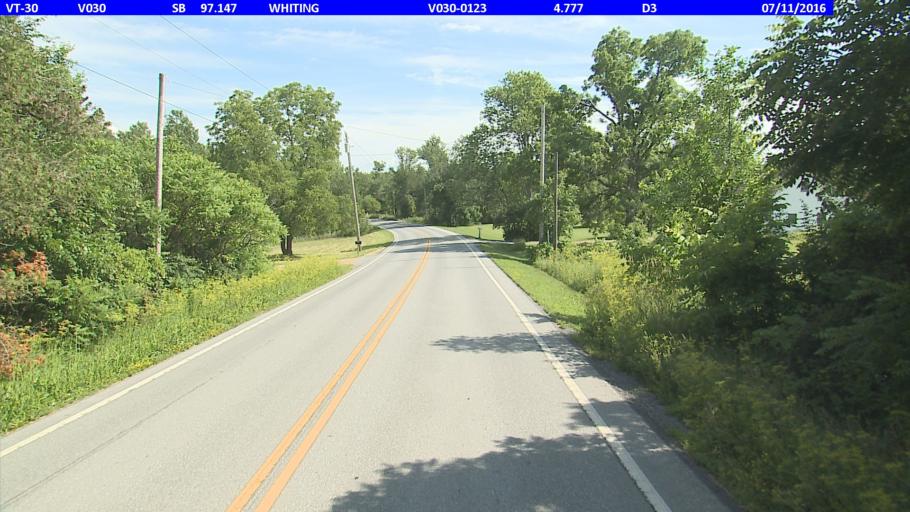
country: US
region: Vermont
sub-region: Addison County
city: Middlebury (village)
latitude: 43.9056
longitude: -73.2081
